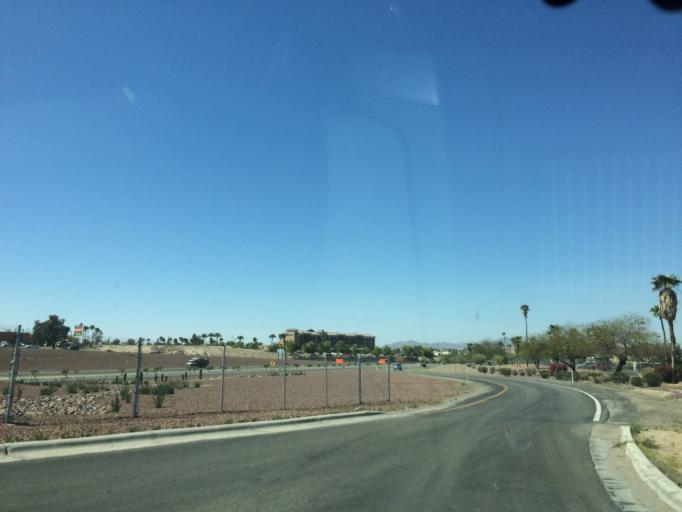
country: US
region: Arizona
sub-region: Yuma County
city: Yuma
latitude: 32.6988
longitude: -114.6066
